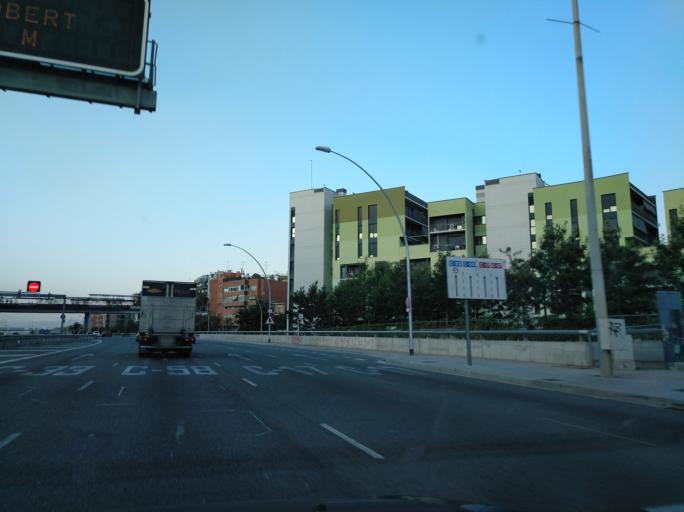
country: ES
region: Catalonia
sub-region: Provincia de Barcelona
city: Nou Barris
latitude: 41.4494
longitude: 2.1887
